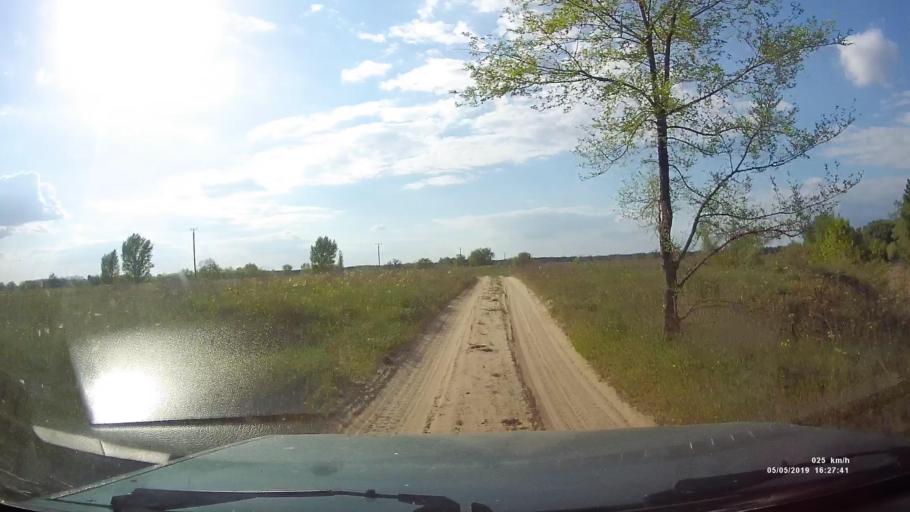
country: RU
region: Rostov
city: Ust'-Donetskiy
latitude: 47.7652
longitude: 41.0173
